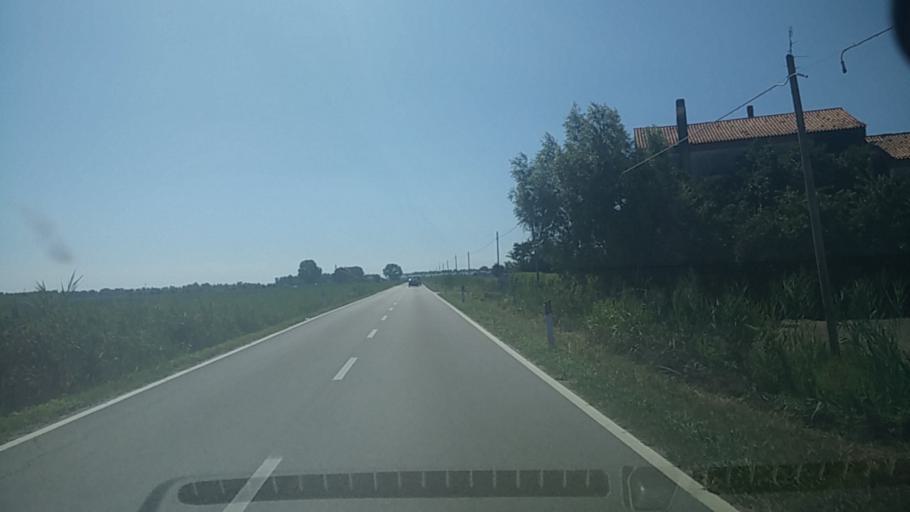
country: IT
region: Veneto
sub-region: Provincia di Venezia
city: La Salute di Livenza
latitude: 45.6343
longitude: 12.8325
